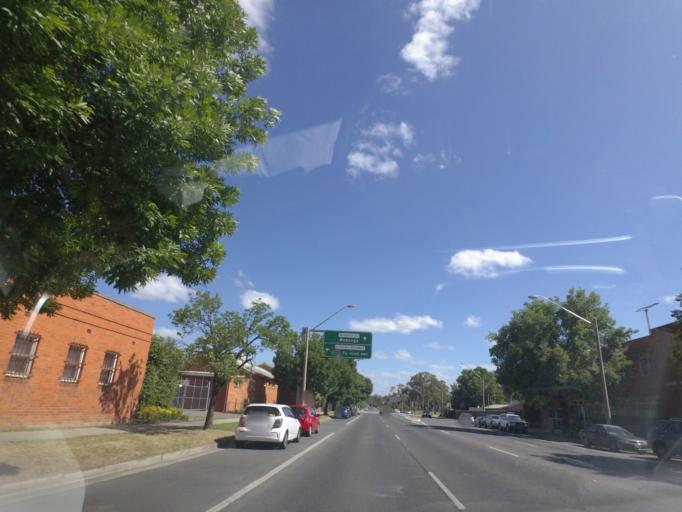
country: AU
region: New South Wales
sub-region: Albury Municipality
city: South Albury
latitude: -36.0828
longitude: 146.9101
